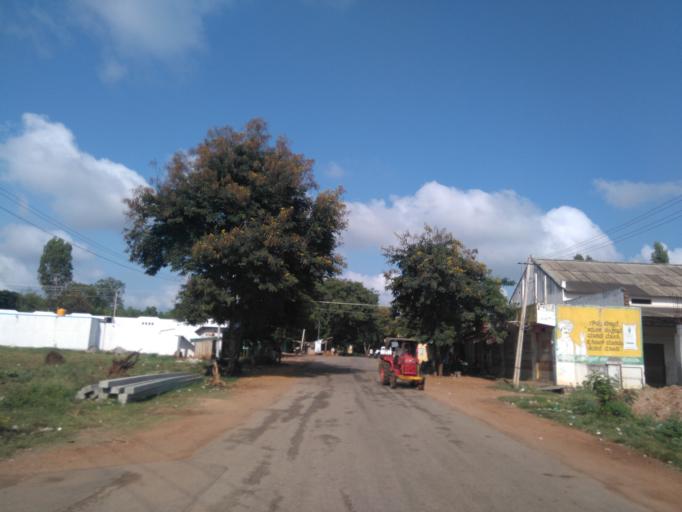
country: IN
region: Karnataka
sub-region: Mysore
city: Tirumakudal Narsipur
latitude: 12.2569
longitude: 76.9623
